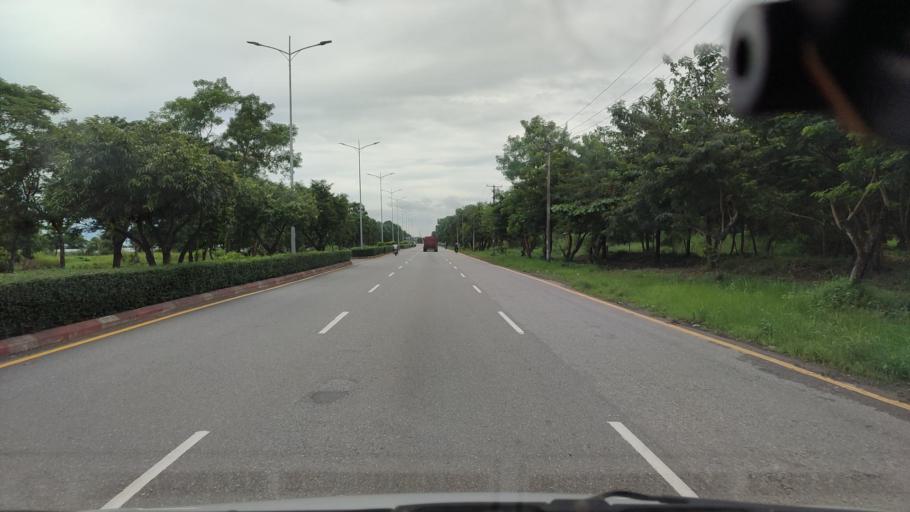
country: MM
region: Bago
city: Thanatpin
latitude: 17.0603
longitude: 96.1585
